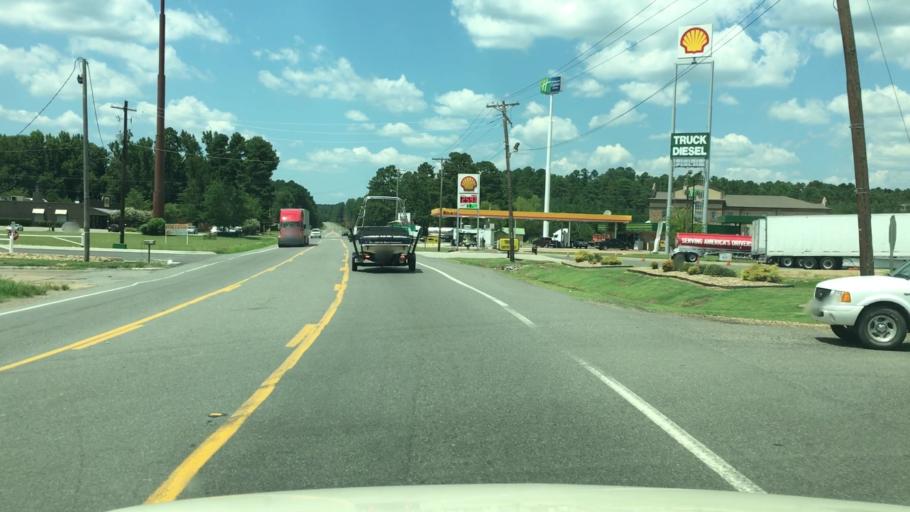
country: US
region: Arkansas
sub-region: Clark County
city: Arkadelphia
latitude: 34.1865
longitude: -93.0711
